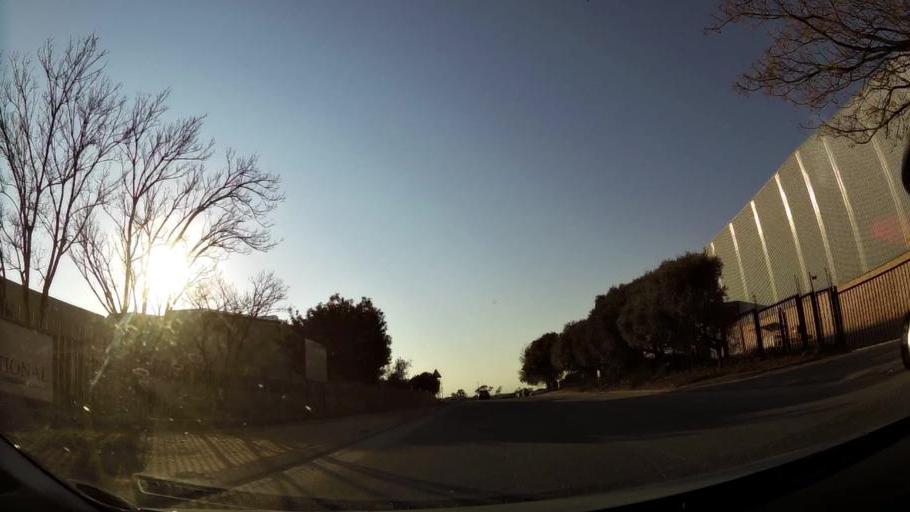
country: ZA
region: Gauteng
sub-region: City of Johannesburg Metropolitan Municipality
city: Modderfontein
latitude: -26.0825
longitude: 28.0889
